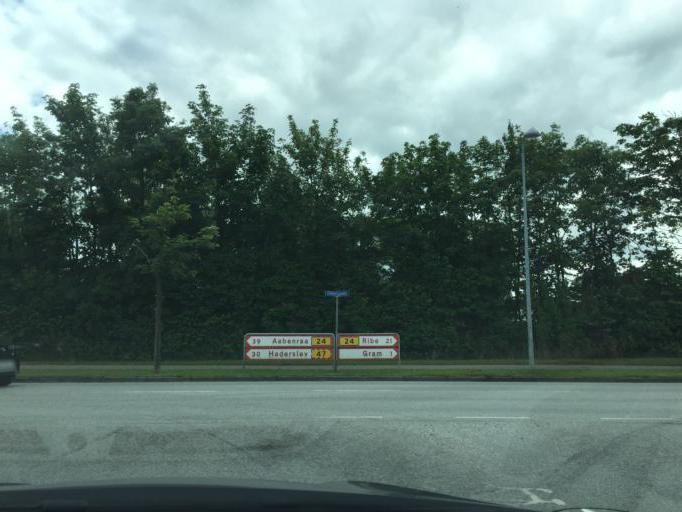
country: DK
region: South Denmark
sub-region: Haderslev Kommune
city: Gram
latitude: 55.2825
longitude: 9.0612
